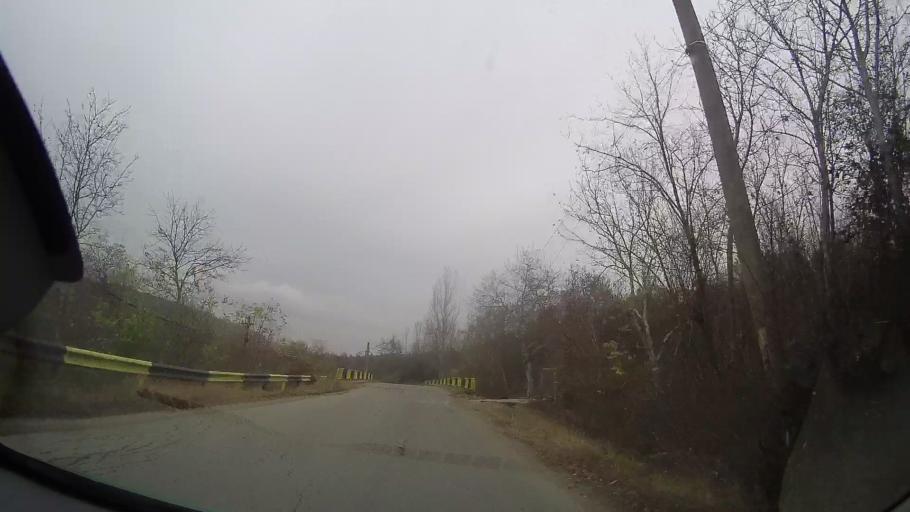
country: RO
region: Prahova
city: Ceptura de Sus
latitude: 45.0496
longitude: 26.3007
